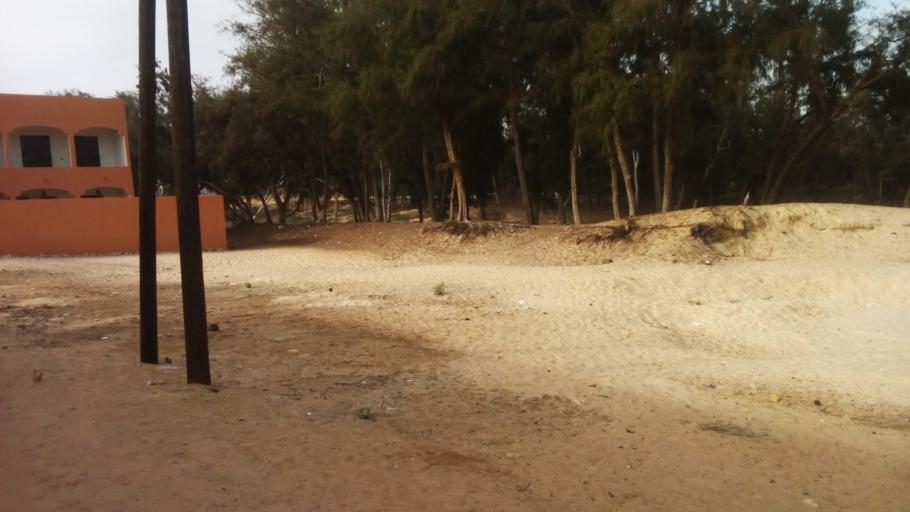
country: SN
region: Dakar
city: Pikine
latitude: 14.8013
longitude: -17.3416
